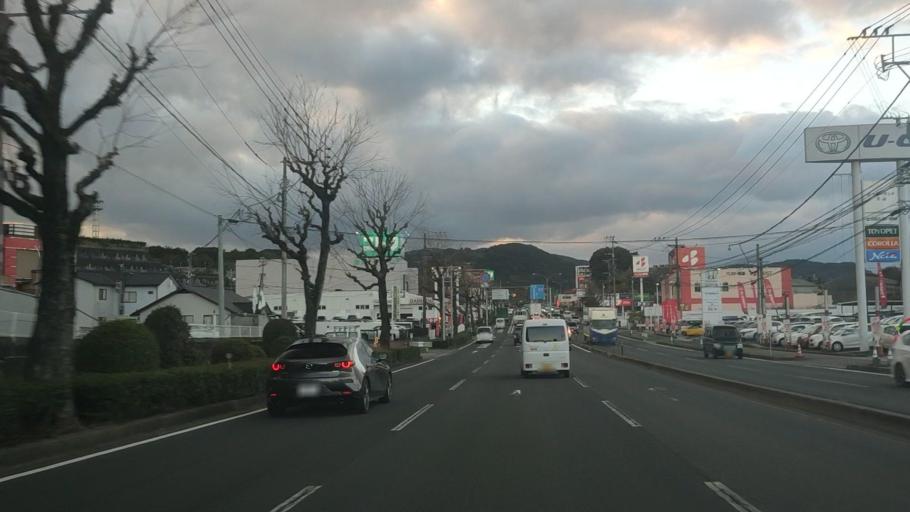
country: JP
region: Nagasaki
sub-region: Isahaya-shi
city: Isahaya
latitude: 32.8295
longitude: 129.9934
